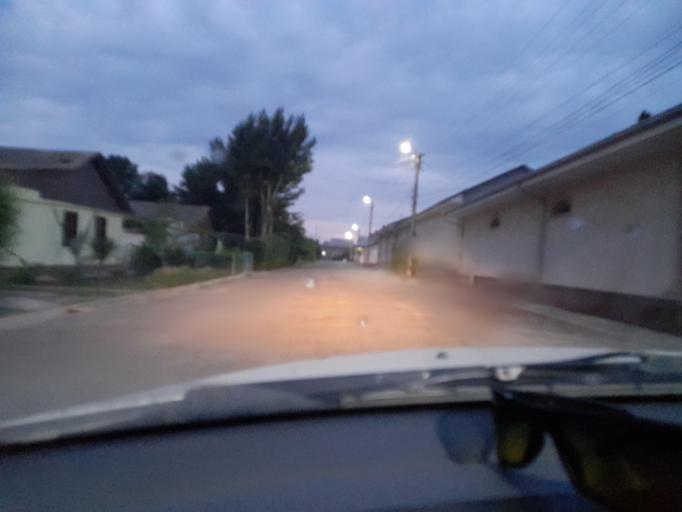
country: UZ
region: Sirdaryo
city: Guliston
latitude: 40.5032
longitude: 68.7810
